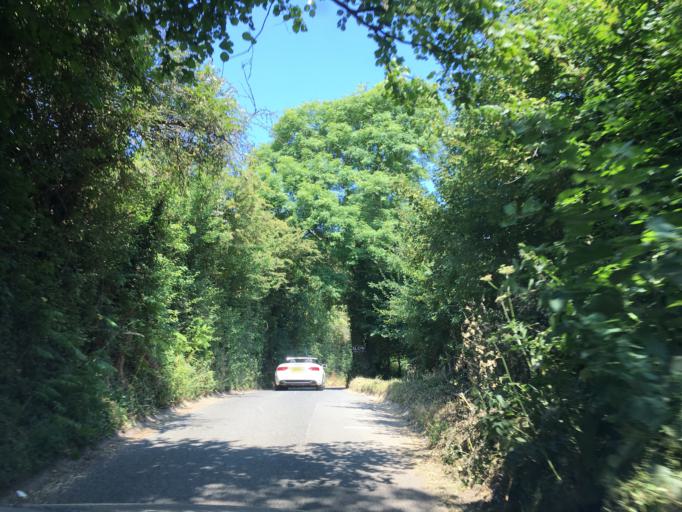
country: GB
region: England
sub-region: Isle of Wight
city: Newchurch
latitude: 50.6785
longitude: -1.2148
